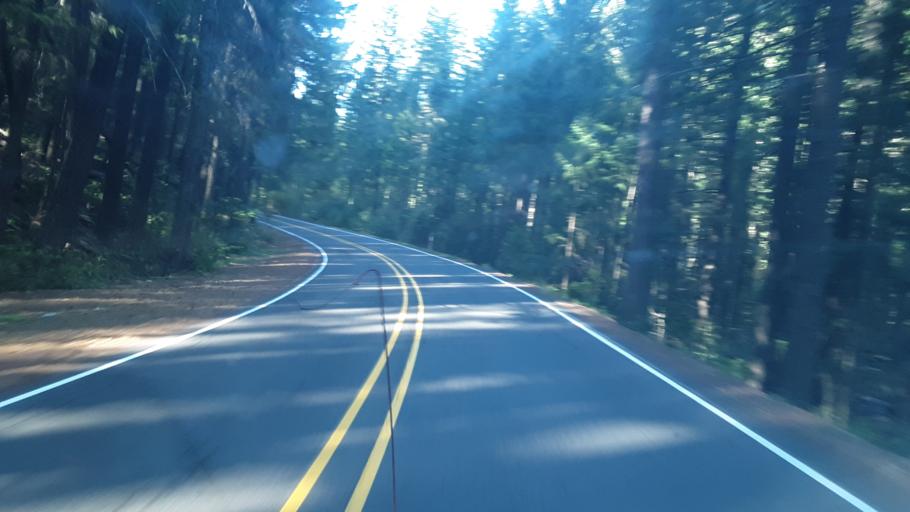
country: US
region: Oregon
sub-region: Jackson County
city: Shady Cove
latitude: 42.9355
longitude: -122.4211
